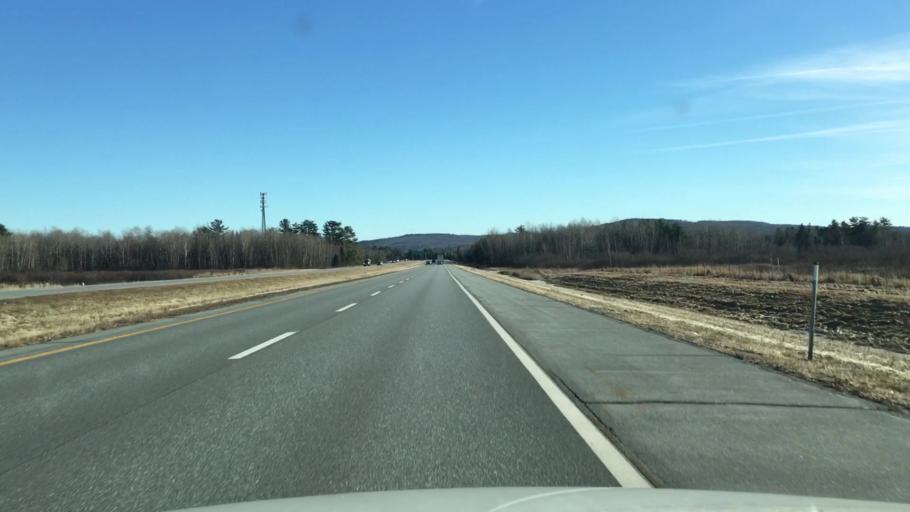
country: US
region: Maine
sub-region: Penobscot County
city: Brewer
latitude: 44.7734
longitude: -68.7453
